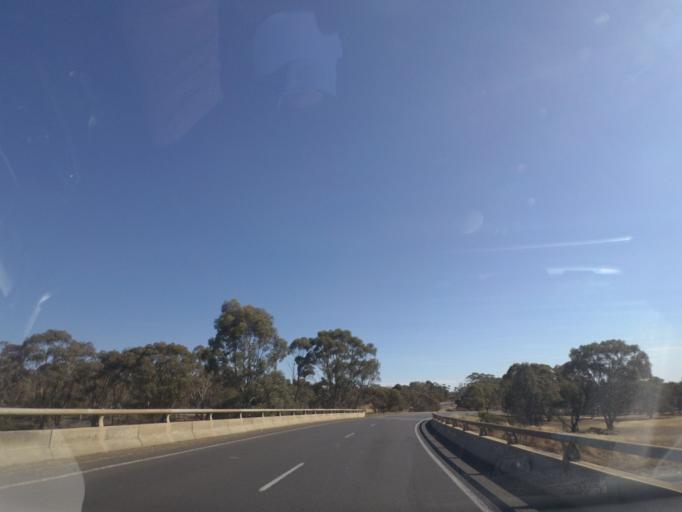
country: AU
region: Victoria
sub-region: Murrindindi
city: Kinglake West
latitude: -36.9836
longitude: 145.1458
